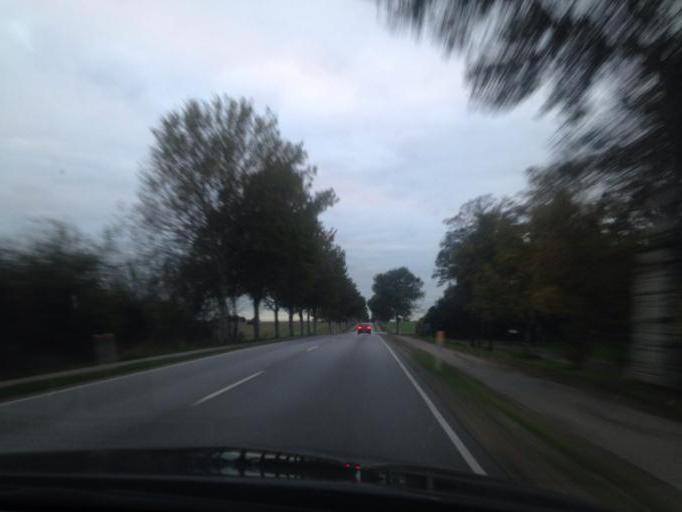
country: DK
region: Zealand
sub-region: Solrod Kommune
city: Havdrup
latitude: 55.5612
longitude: 12.1398
